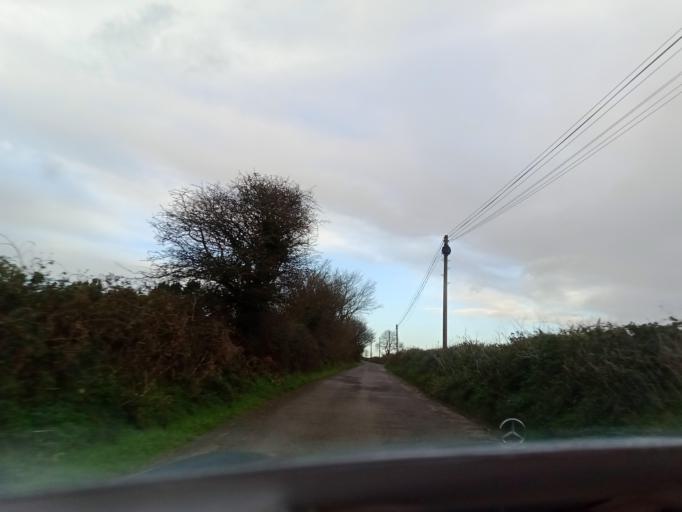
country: IE
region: Munster
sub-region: Waterford
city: Waterford
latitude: 52.3352
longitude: -7.0361
